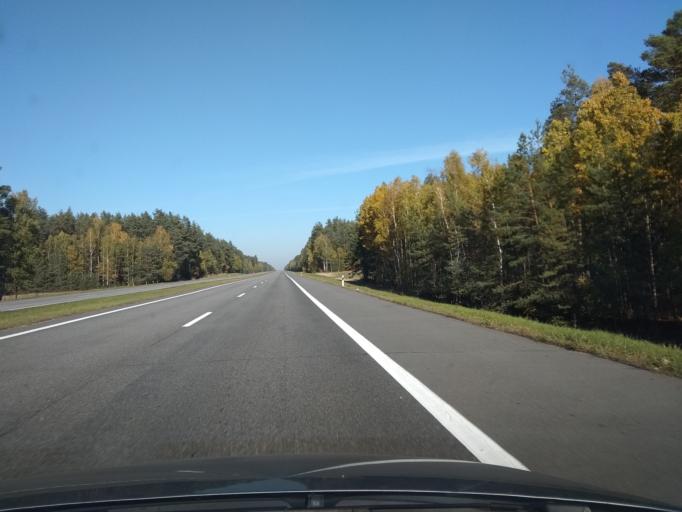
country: BY
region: Grodnenskaya
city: Zhyrovichy
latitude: 52.8724
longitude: 25.6588
